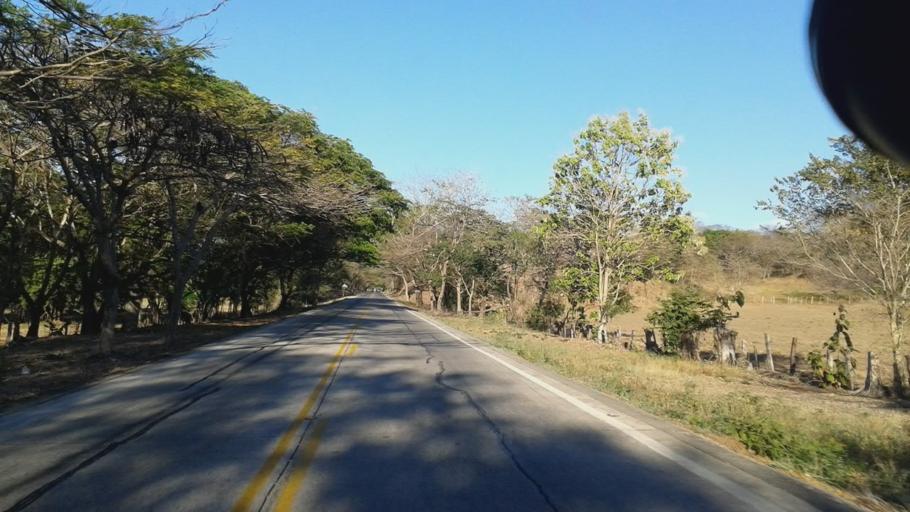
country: CR
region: Guanacaste
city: Nandayure
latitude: 10.2224
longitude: -85.1604
